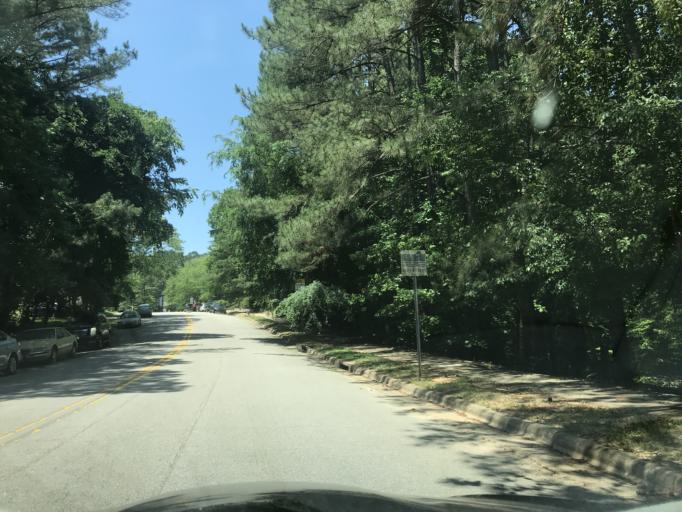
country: US
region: North Carolina
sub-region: Wake County
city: West Raleigh
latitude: 35.8630
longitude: -78.6518
